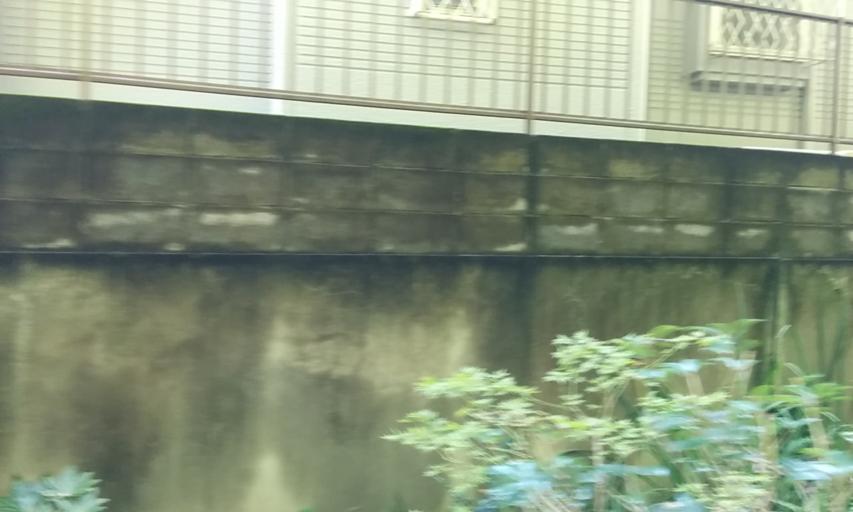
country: JP
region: Tokyo
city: Kokubunji
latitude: 35.6935
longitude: 139.4743
